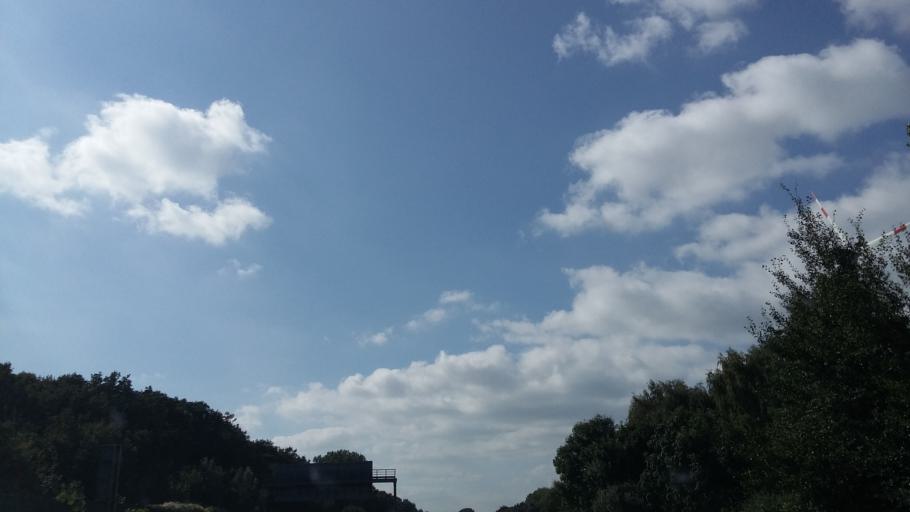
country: DE
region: Bremen
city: Bremen
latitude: 53.1195
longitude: 8.7962
